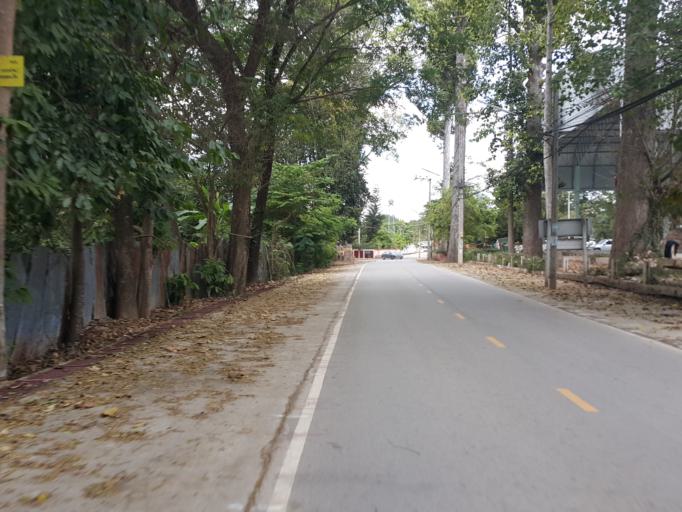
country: TH
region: Chiang Mai
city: San Sai
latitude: 18.8681
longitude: 99.1372
